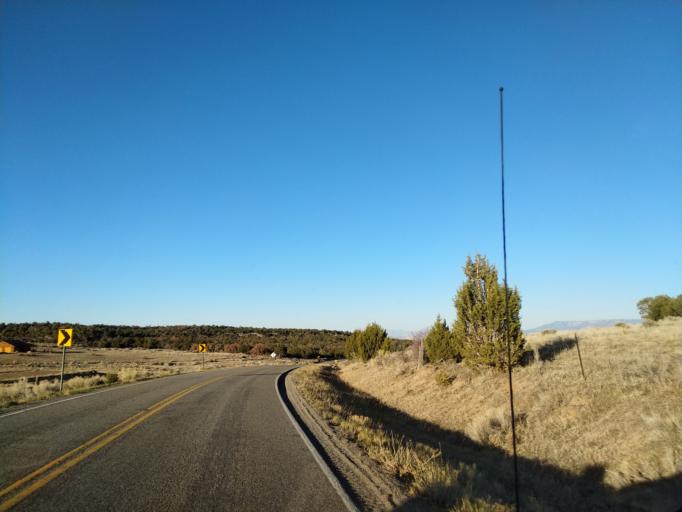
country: US
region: Colorado
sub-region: Mesa County
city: Redlands
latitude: 39.0027
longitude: -108.7082
